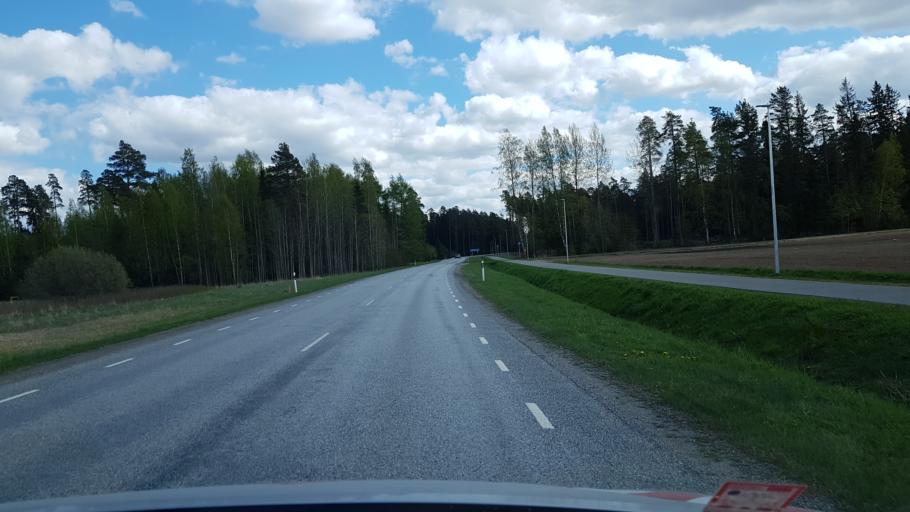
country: EE
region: Tartu
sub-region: UElenurme vald
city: Ulenurme
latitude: 58.3209
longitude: 26.8289
